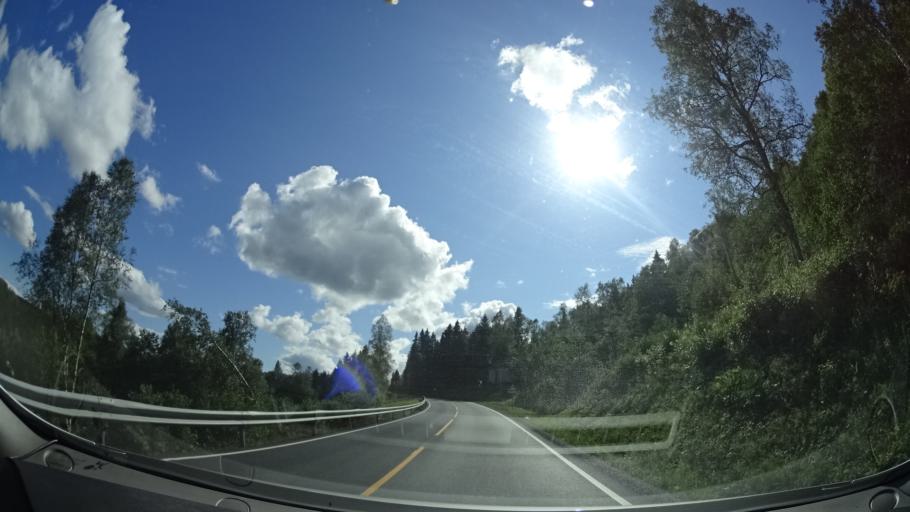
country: NO
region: Sor-Trondelag
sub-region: Snillfjord
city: Krokstadora
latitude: 63.2415
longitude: 9.5965
